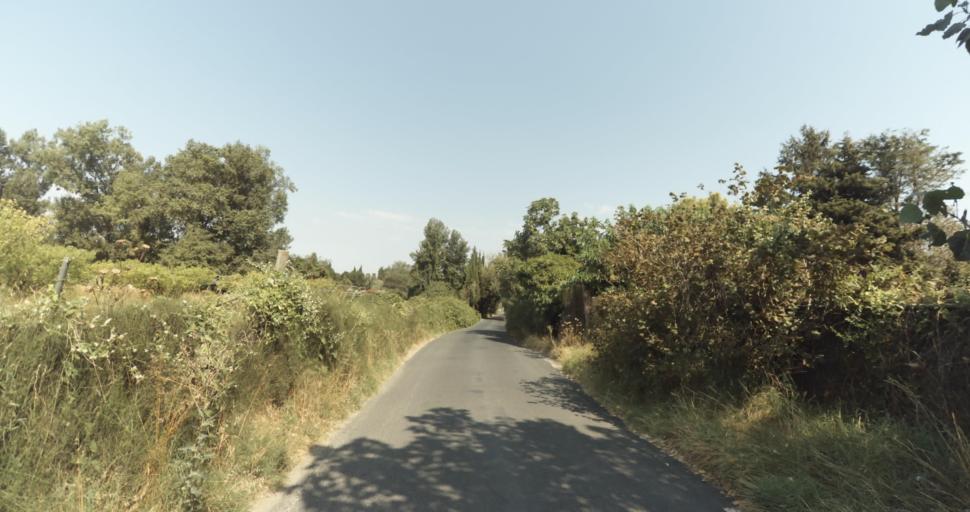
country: FR
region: Languedoc-Roussillon
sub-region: Departement des Pyrenees-Orientales
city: Elne
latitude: 42.6167
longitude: 2.9838
